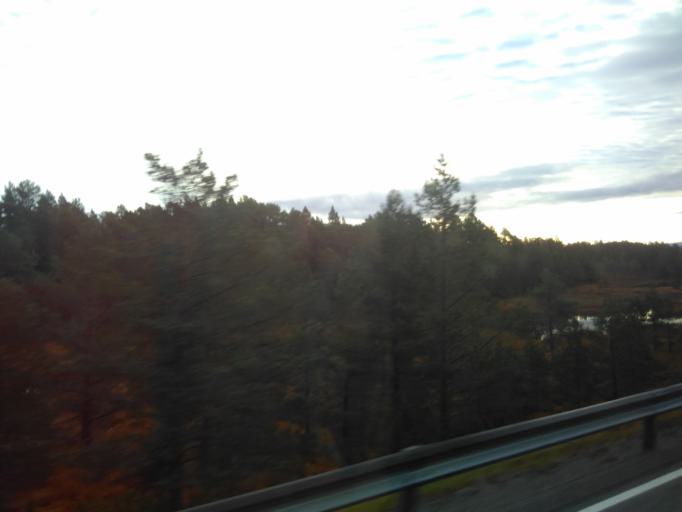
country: NO
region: Sor-Trondelag
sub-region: Hitra
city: Fillan
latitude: 63.5407
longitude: 9.0604
